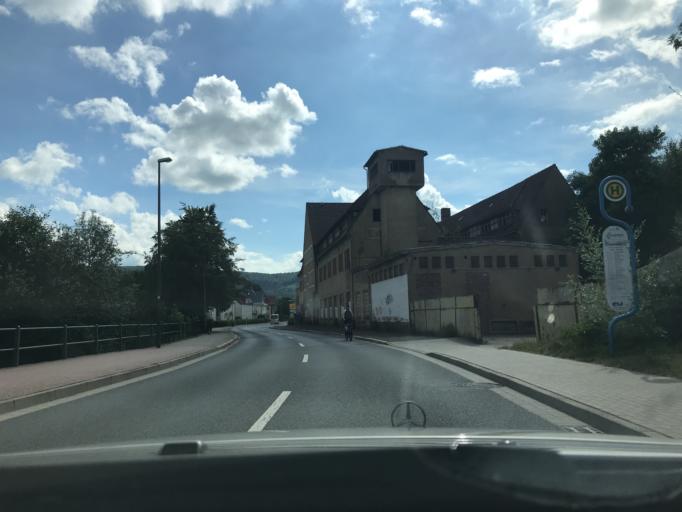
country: DE
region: Thuringia
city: Heilbad Heiligenstadt
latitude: 51.3785
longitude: 10.1282
